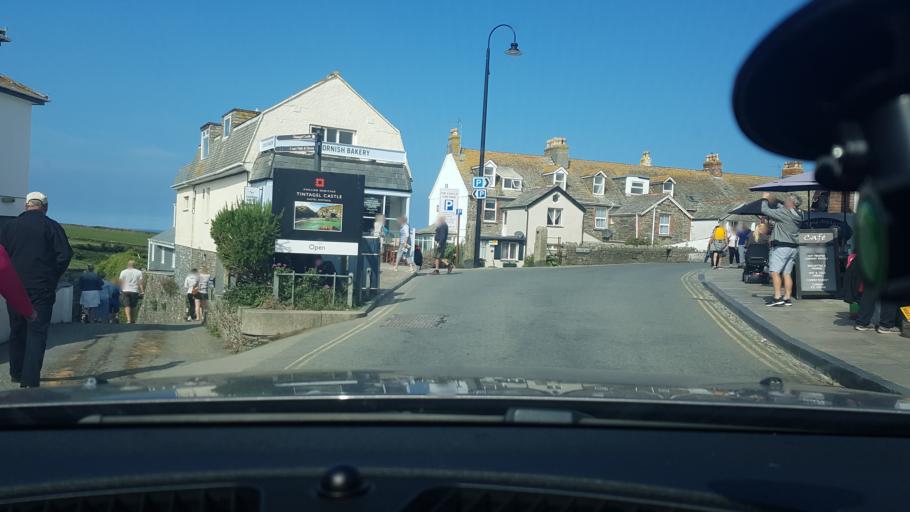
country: GB
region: England
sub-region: Cornwall
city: Tintagel
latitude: 50.6641
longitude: -4.7532
